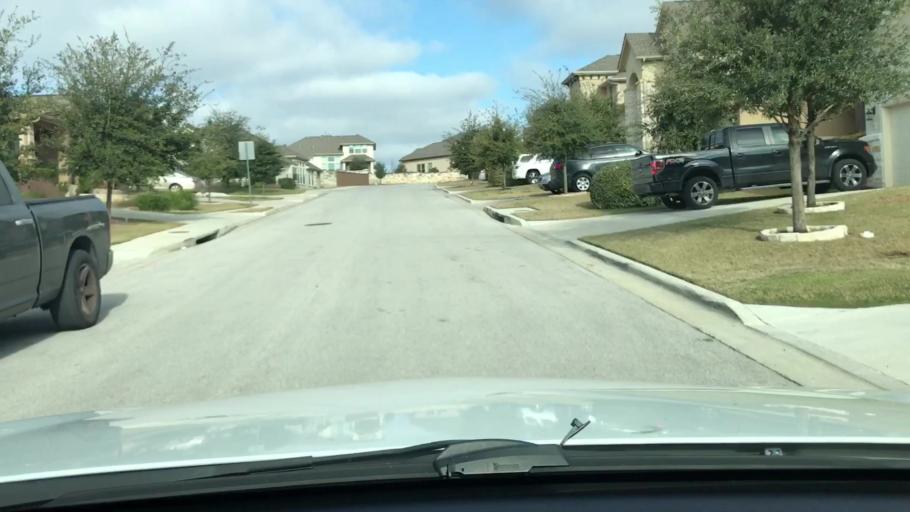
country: US
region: Texas
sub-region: Travis County
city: Bee Cave
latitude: 30.3145
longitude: -97.9587
